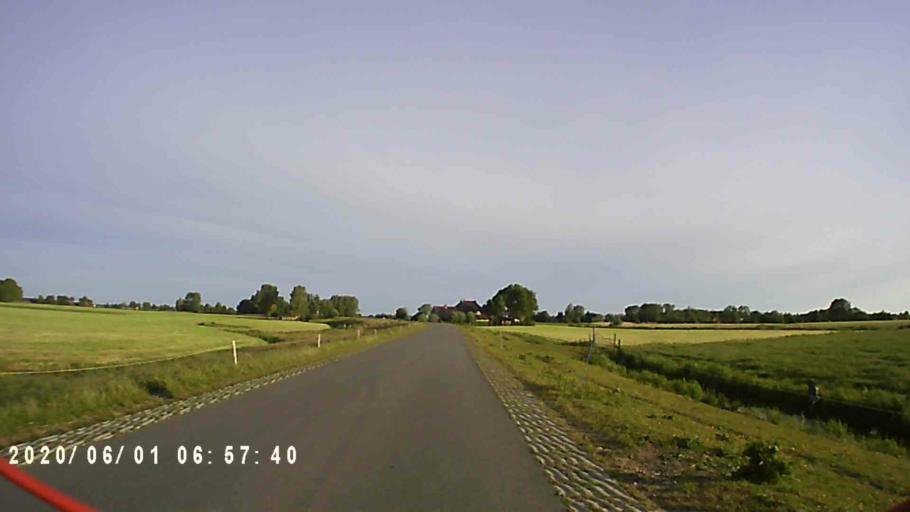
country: NL
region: Friesland
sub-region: Gemeente Dongeradeel
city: Anjum
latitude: 53.3185
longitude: 6.1057
